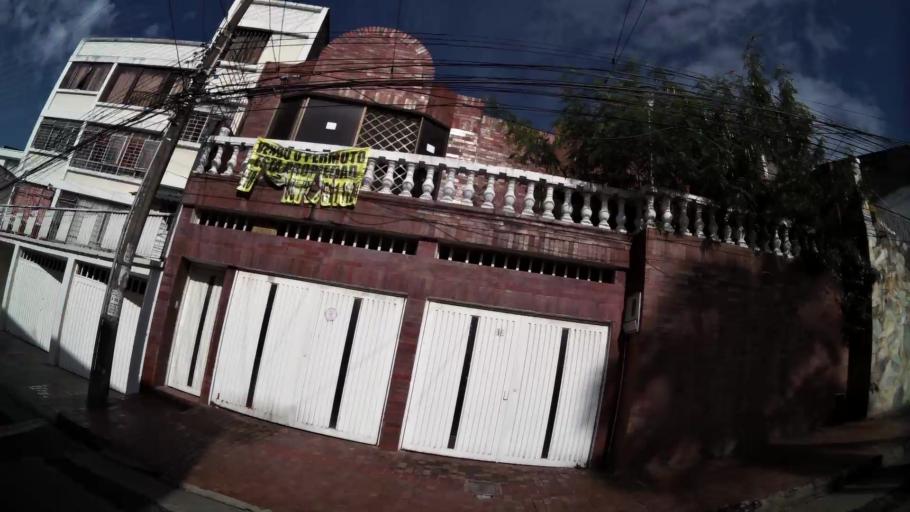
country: CO
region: Valle del Cauca
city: Cali
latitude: 3.4386
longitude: -76.5425
